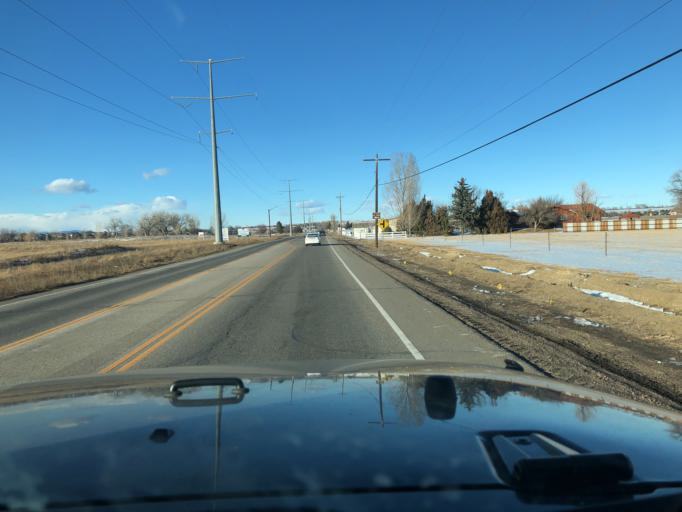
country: US
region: Colorado
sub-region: Boulder County
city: Longmont
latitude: 40.1859
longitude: -105.0551
